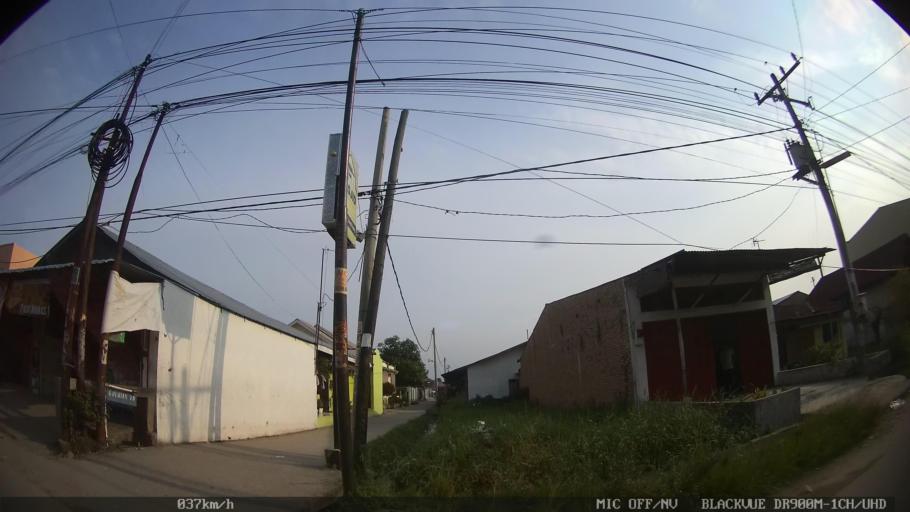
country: ID
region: North Sumatra
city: Medan
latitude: 3.5852
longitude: 98.7474
